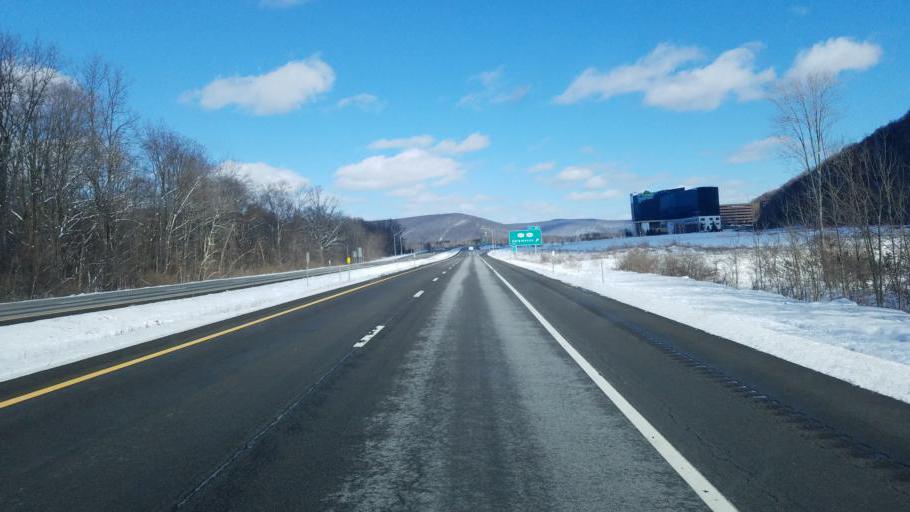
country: US
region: New York
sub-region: Cattaraugus County
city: Salamanca
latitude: 42.1514
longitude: -78.7603
